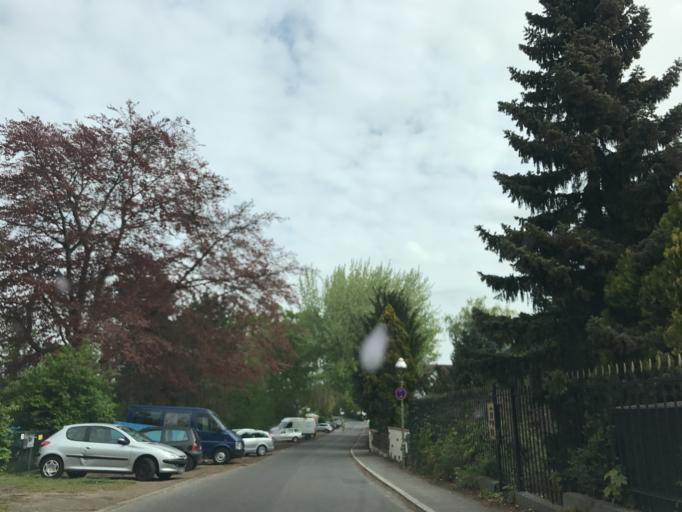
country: DE
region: Berlin
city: Wilhelmstadt
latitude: 52.5090
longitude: 13.1881
